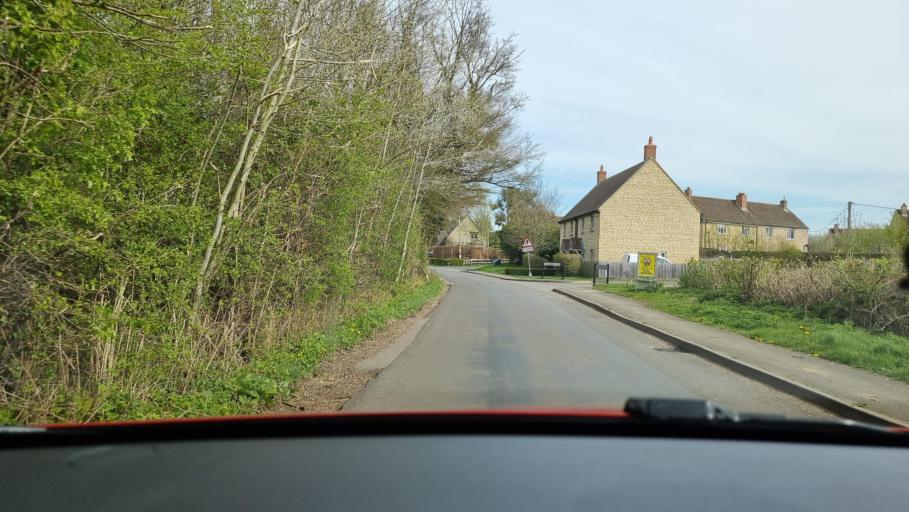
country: GB
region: England
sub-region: Oxfordshire
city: Kidlington
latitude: 51.8622
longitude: -1.2333
